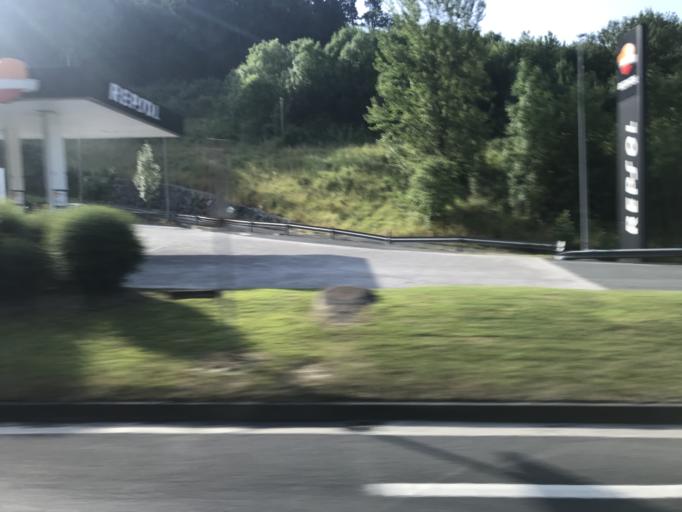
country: ES
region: Basque Country
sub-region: Provincia de Guipuzcoa
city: Arama
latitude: 43.0655
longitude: -2.1644
